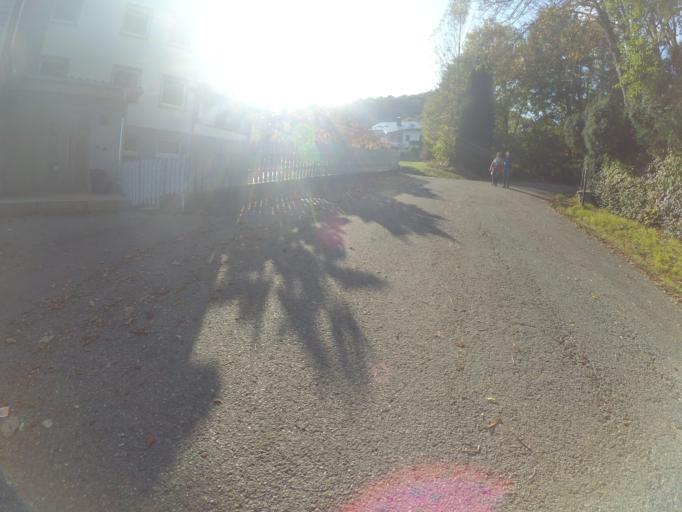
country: DE
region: Baden-Wuerttemberg
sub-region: Regierungsbezirk Stuttgart
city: Heubach
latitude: 48.7851
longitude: 9.9291
